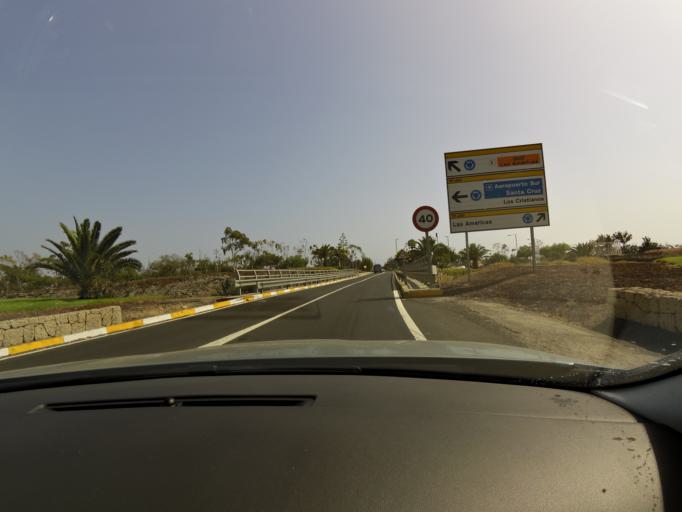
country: ES
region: Canary Islands
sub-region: Provincia de Santa Cruz de Tenerife
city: Playa de las Americas
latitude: 28.0668
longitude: -16.7202
